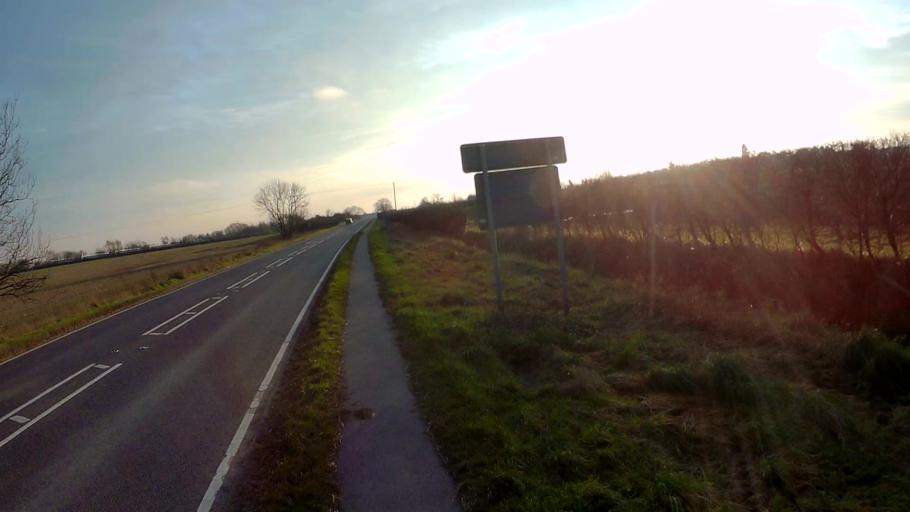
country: GB
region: England
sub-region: Lincolnshire
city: Bourne
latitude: 52.7877
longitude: -0.3766
